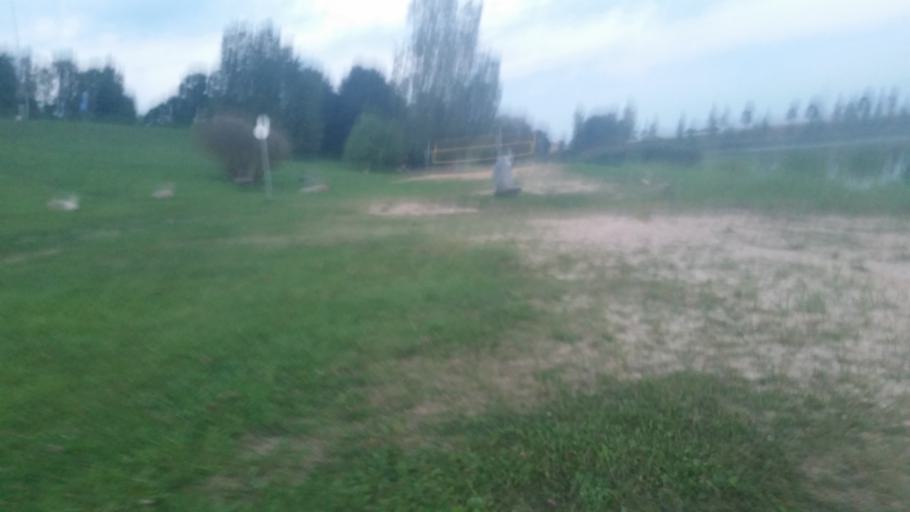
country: LV
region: Ogre
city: Ogre
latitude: 56.8133
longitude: 24.5943
